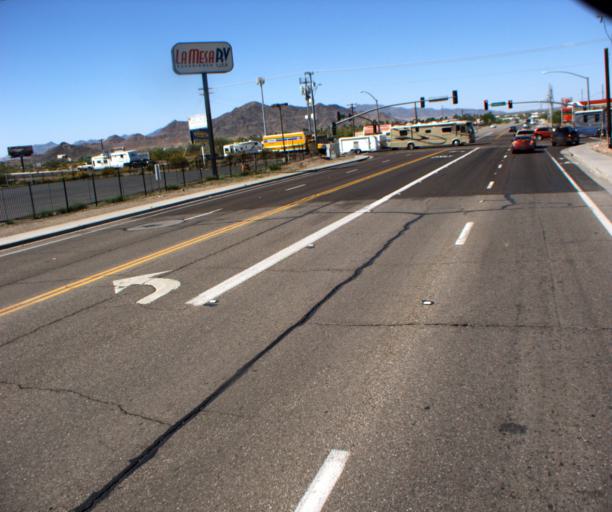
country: US
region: Arizona
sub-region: La Paz County
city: Quartzsite
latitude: 33.6669
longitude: -114.2161
